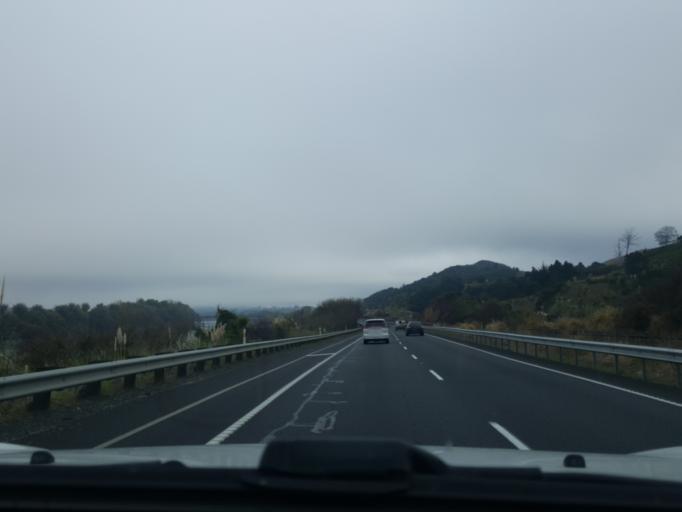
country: NZ
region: Auckland
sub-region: Auckland
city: Pukekohe East
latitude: -37.2886
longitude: 175.0545
